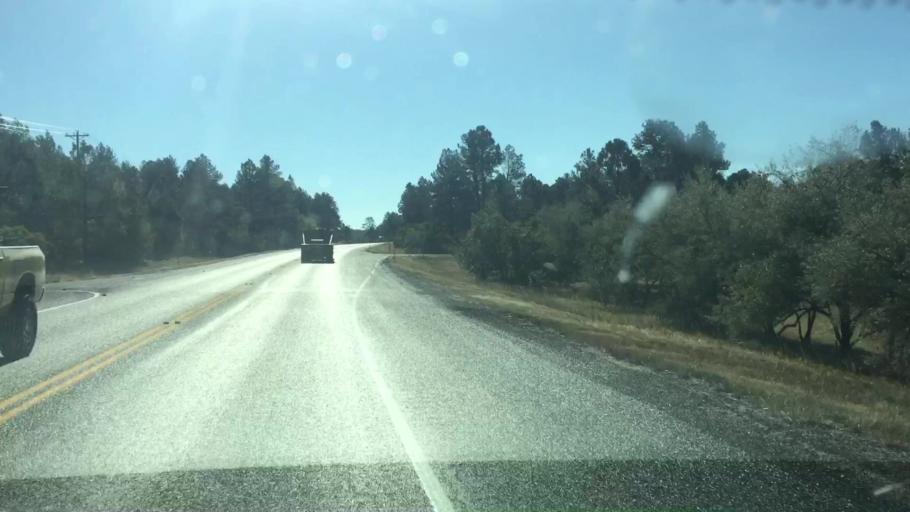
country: US
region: Colorado
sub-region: Douglas County
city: The Pinery
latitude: 39.3830
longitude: -104.7255
